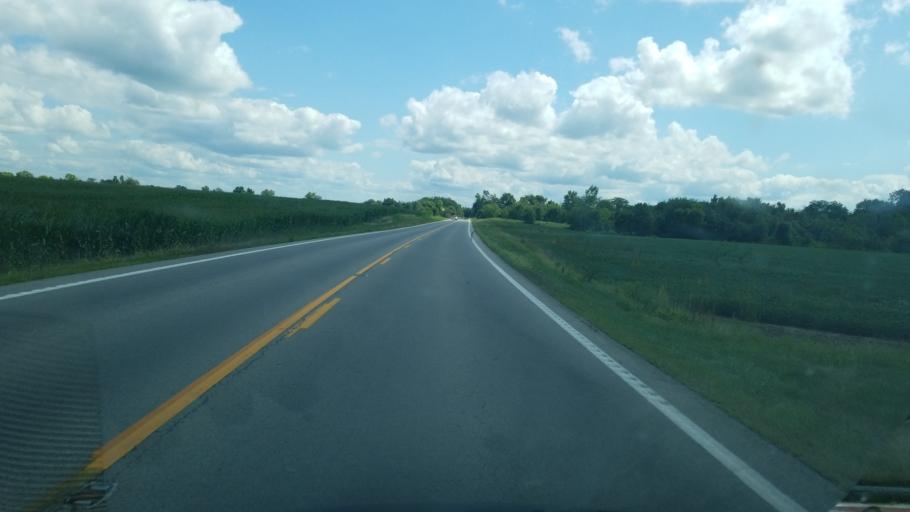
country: US
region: Ohio
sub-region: Putnam County
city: Kalida
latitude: 40.9460
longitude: -84.1618
